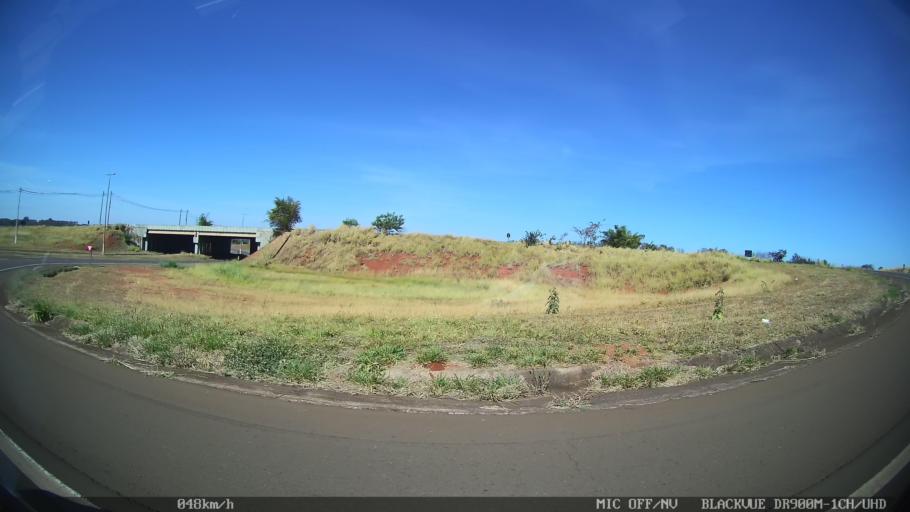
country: BR
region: Sao Paulo
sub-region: Barretos
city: Barretos
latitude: -20.5268
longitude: -48.5913
